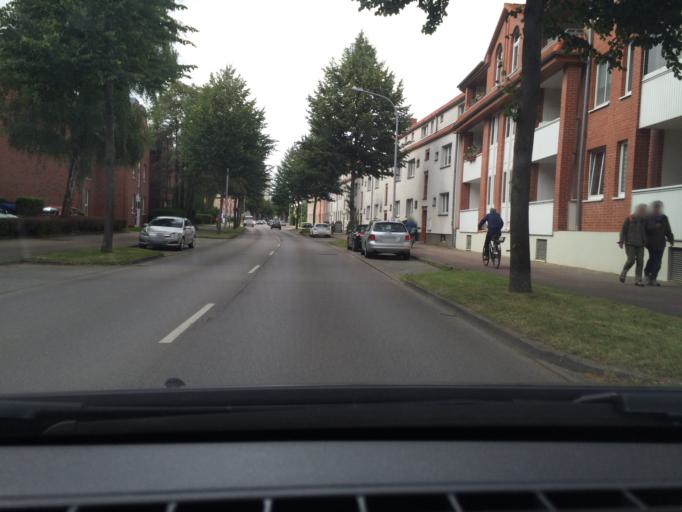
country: DE
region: Mecklenburg-Vorpommern
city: Stralsund
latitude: 54.3252
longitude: 13.0765
